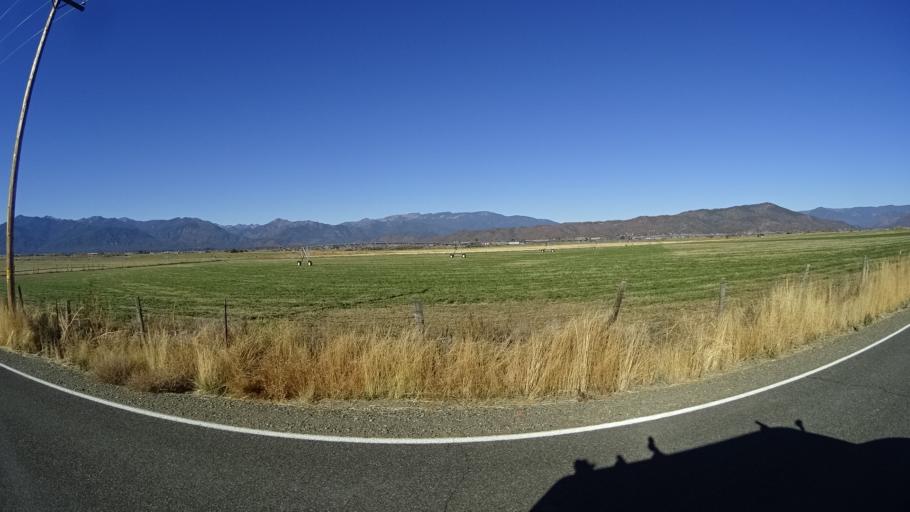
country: US
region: California
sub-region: Siskiyou County
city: Yreka
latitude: 41.5415
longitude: -122.8308
